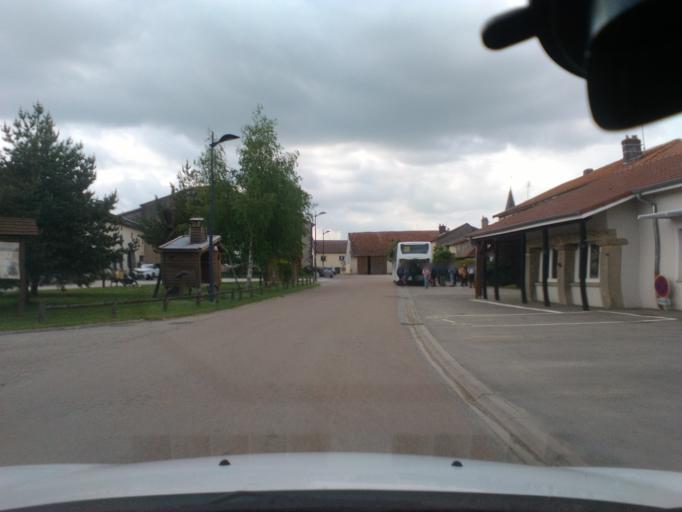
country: FR
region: Lorraine
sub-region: Departement des Vosges
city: Mirecourt
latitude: 48.3340
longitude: 6.0977
